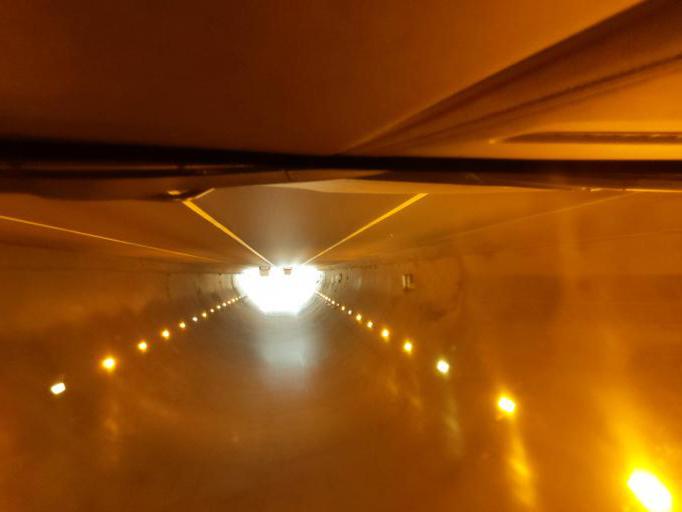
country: CN
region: Fujian
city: Yingcun
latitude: 24.6460
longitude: 118.0890
